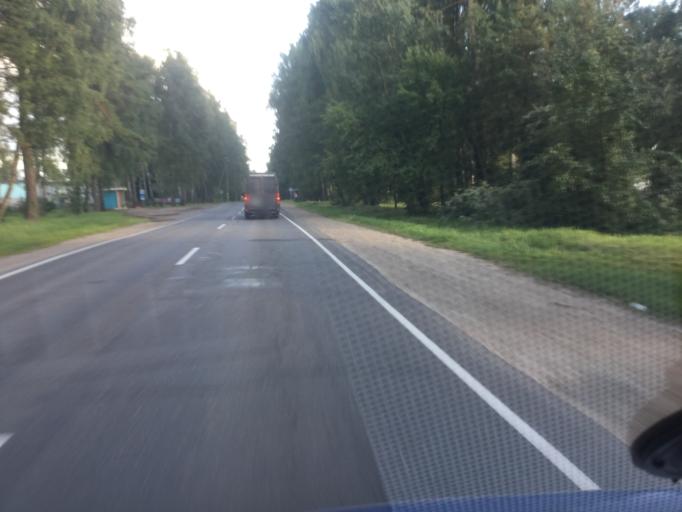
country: BY
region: Vitebsk
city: Navapolatsk
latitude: 55.6353
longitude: 28.6331
